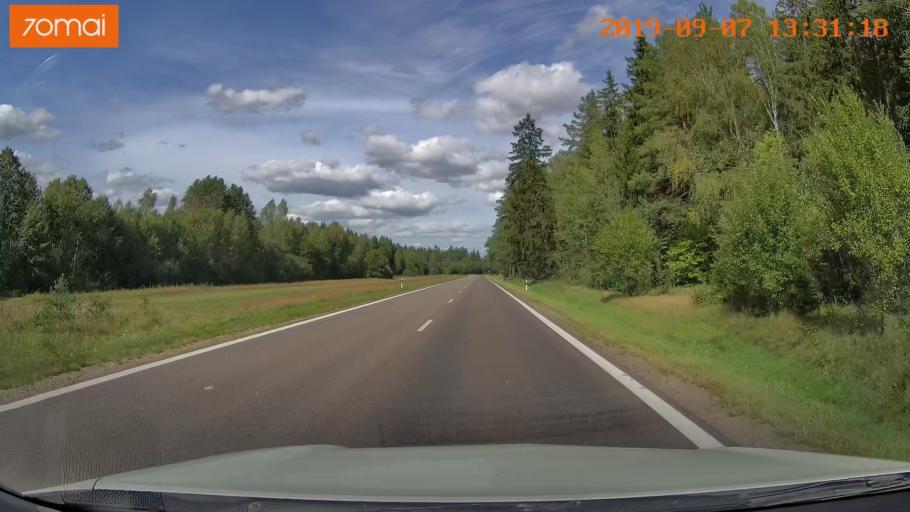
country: LT
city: Salcininkai
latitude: 54.4545
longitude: 25.3233
